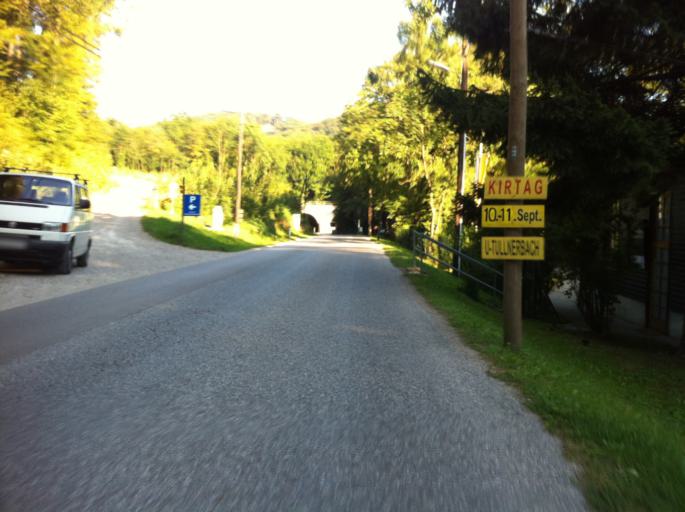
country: AT
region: Lower Austria
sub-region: Politischer Bezirk Wien-Umgebung
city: Wolfsgraben
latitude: 48.1915
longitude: 16.1238
